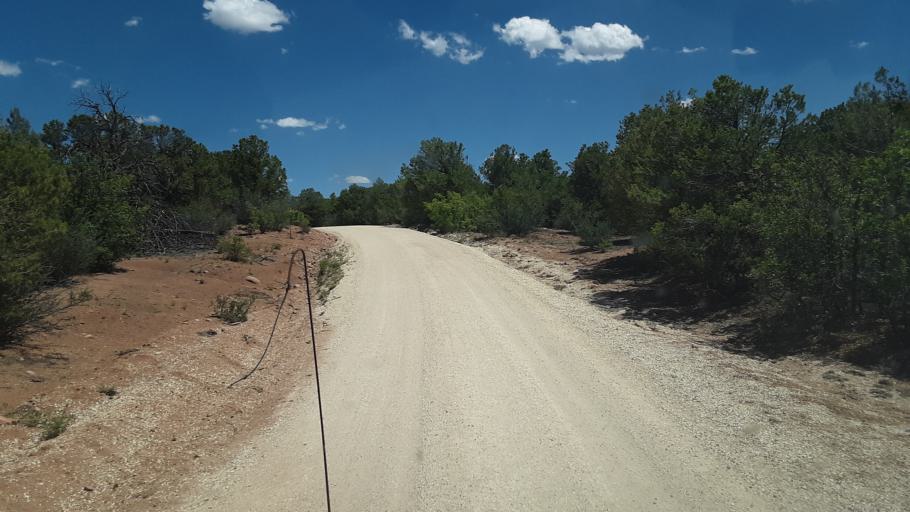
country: US
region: Colorado
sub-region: Custer County
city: Westcliffe
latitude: 38.3264
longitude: -105.6290
